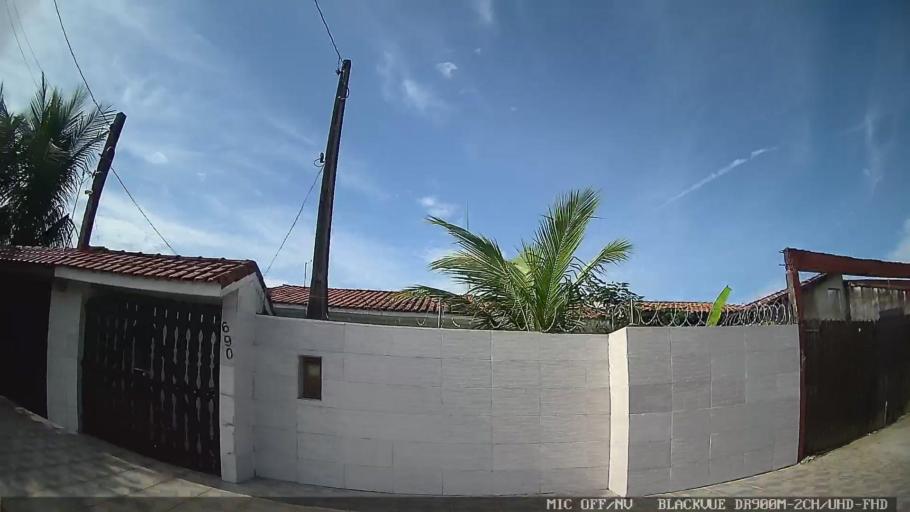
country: BR
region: Sao Paulo
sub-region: Itanhaem
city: Itanhaem
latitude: -24.1616
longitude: -46.7690
